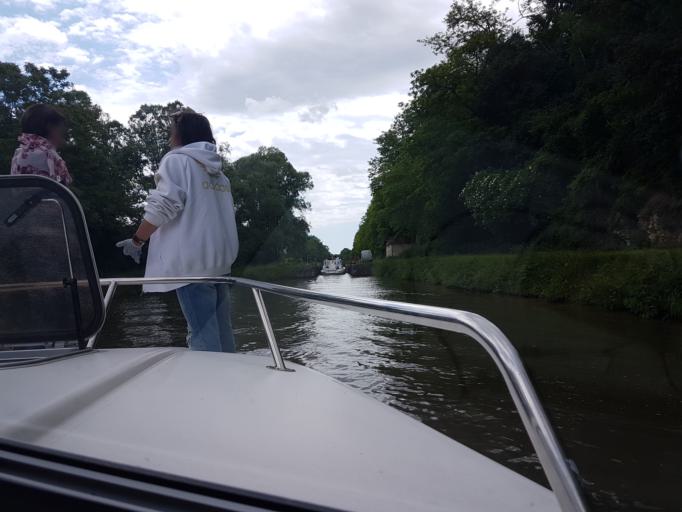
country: FR
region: Bourgogne
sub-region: Departement de la Nievre
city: Clamecy
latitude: 47.4882
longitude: 3.5244
